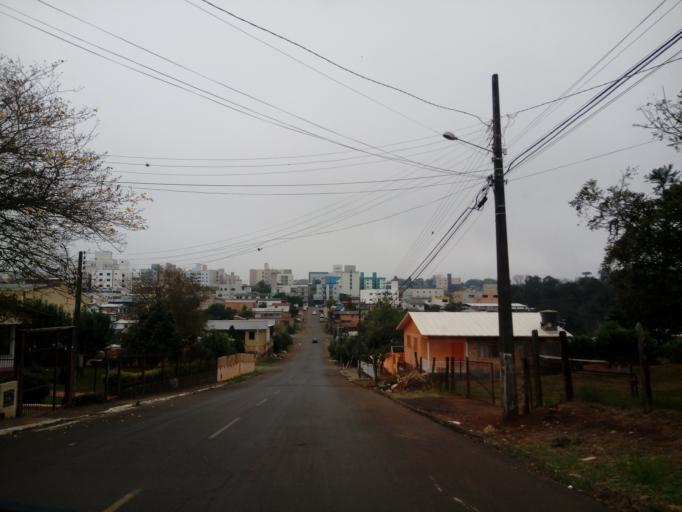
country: BR
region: Santa Catarina
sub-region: Chapeco
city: Chapeco
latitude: -27.0990
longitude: -52.6689
